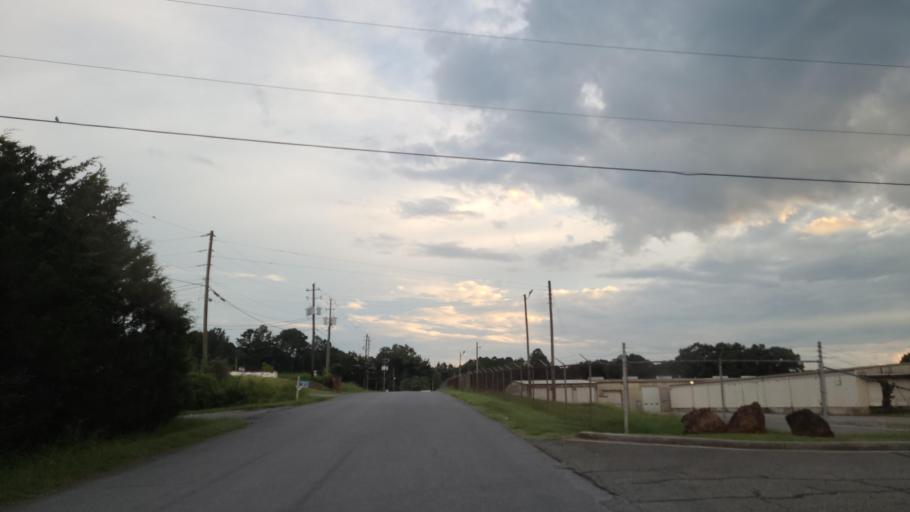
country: US
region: Georgia
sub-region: Bartow County
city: Cartersville
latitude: 34.2179
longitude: -84.7948
